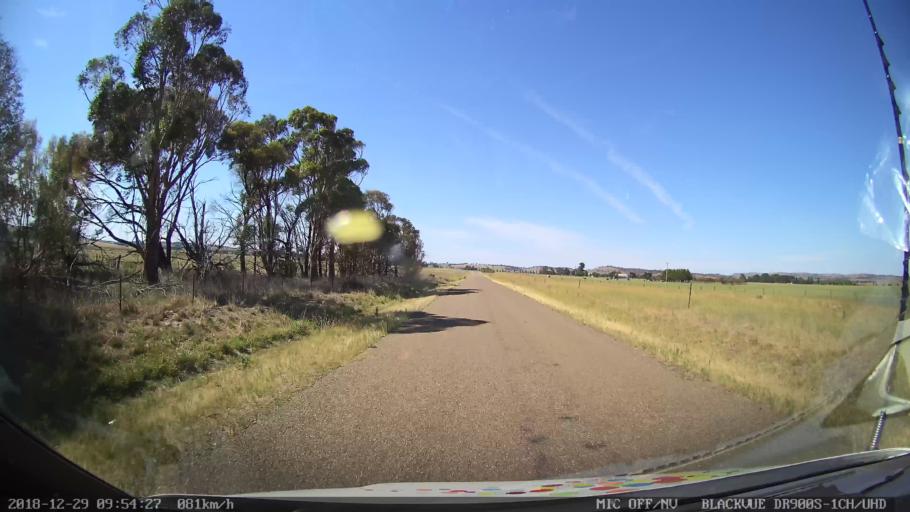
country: AU
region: New South Wales
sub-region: Goulburn Mulwaree
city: Goulburn
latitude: -34.7635
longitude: 149.4669
